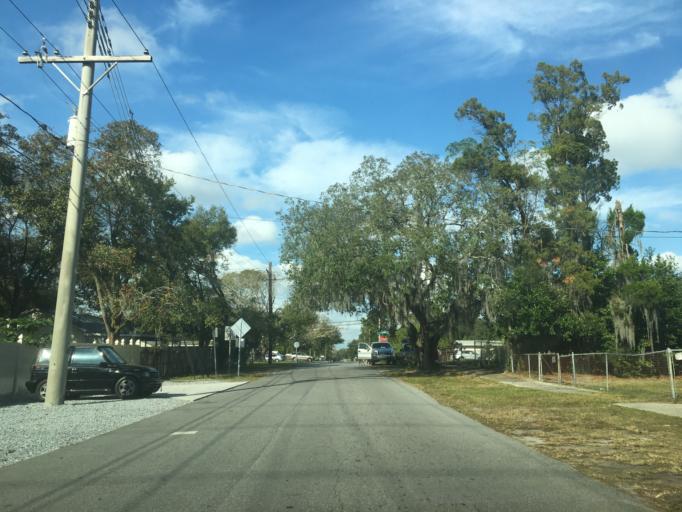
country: US
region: Florida
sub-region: Hillsborough County
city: University
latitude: 28.0393
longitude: -82.4305
